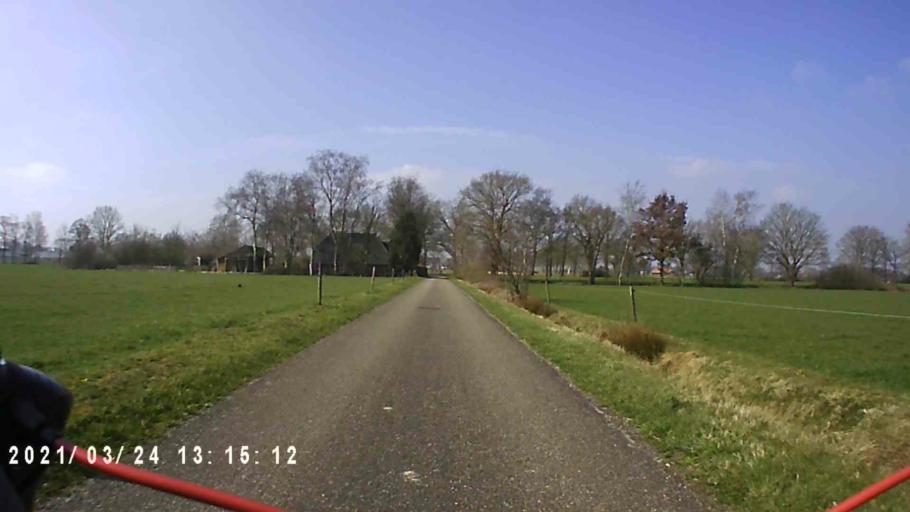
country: NL
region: Groningen
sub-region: Gemeente Leek
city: Leek
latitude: 53.1152
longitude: 6.2919
